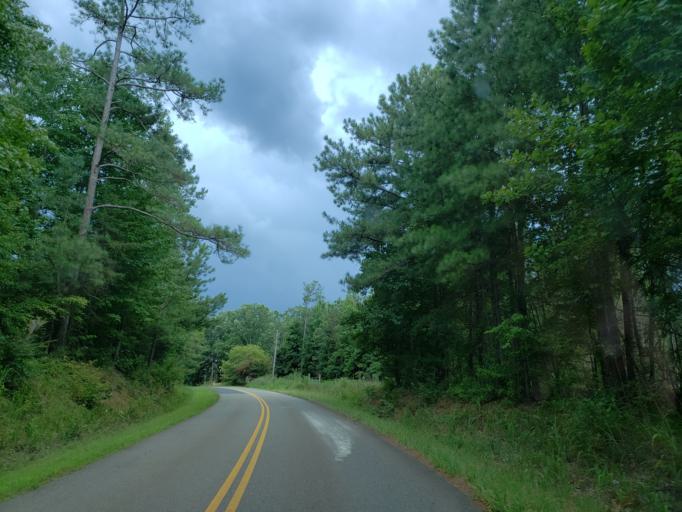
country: US
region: Georgia
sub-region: Pickens County
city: Jasper
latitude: 34.3894
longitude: -84.4665
